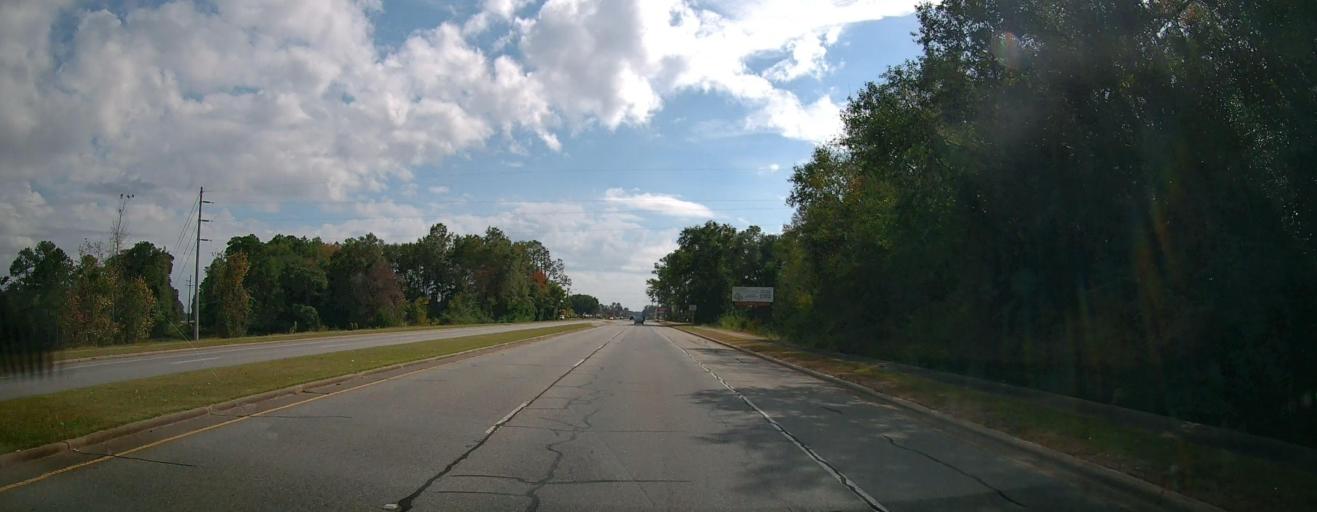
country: US
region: Georgia
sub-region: Mitchell County
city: Camilla
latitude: 31.2410
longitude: -84.2001
